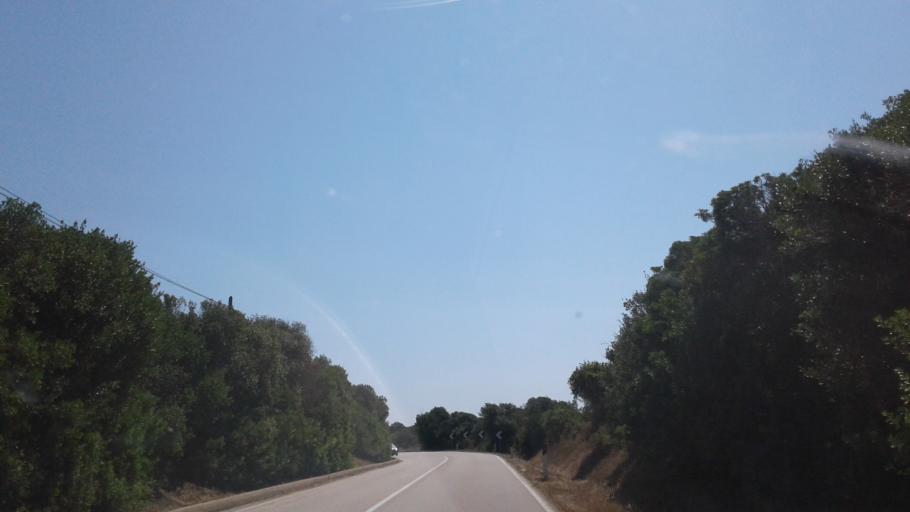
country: IT
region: Sardinia
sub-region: Provincia di Olbia-Tempio
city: Luogosanto
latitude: 41.1266
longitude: 9.2803
